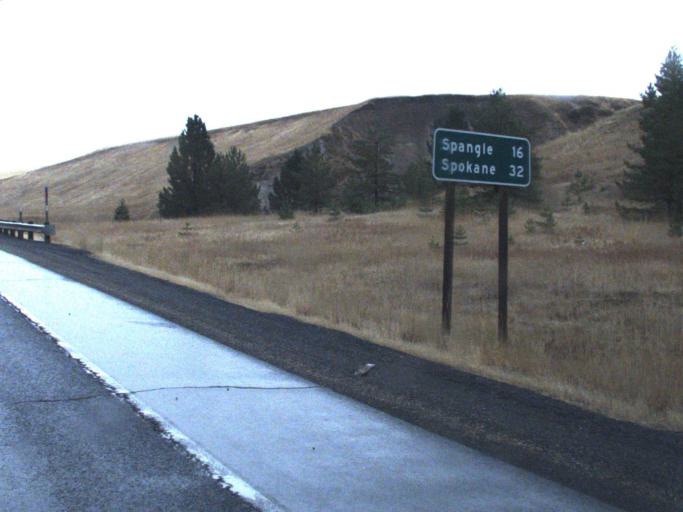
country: US
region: Washington
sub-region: Whitman County
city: Colfax
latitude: 47.2189
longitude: -117.3549
